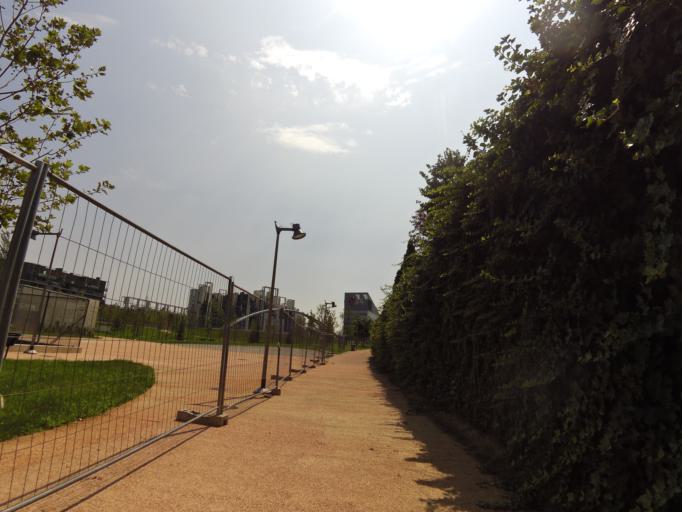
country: IT
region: Lombardy
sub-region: Citta metropolitana di Milano
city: Novate Milanese
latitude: 45.4885
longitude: 9.1451
